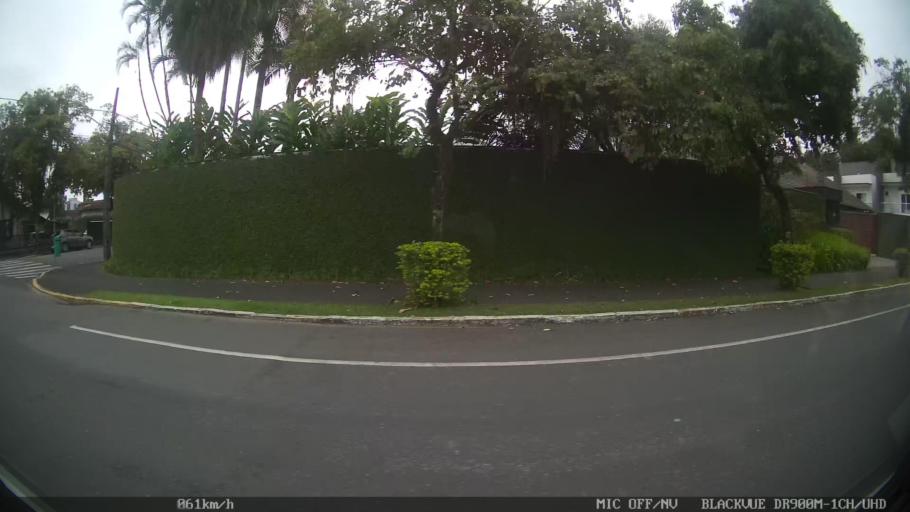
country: BR
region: Santa Catarina
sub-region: Joinville
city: Joinville
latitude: -26.2961
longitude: -48.8541
